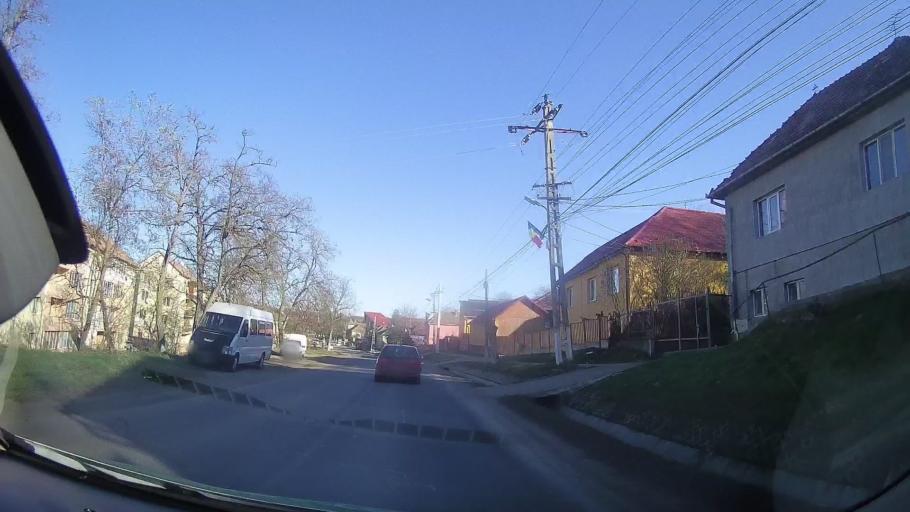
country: RO
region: Mures
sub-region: Comuna Sarmasu
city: Sarmasu
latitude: 46.7509
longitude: 24.1569
